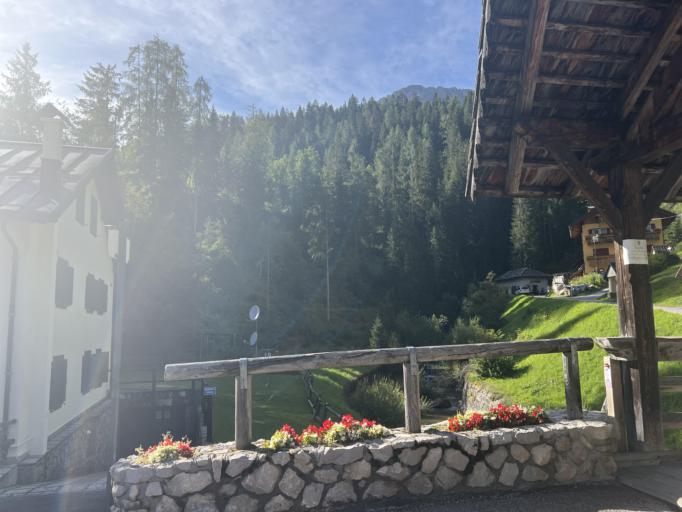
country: IT
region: Veneto
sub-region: Provincia di Belluno
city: Granvilla
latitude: 46.5678
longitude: 12.6878
